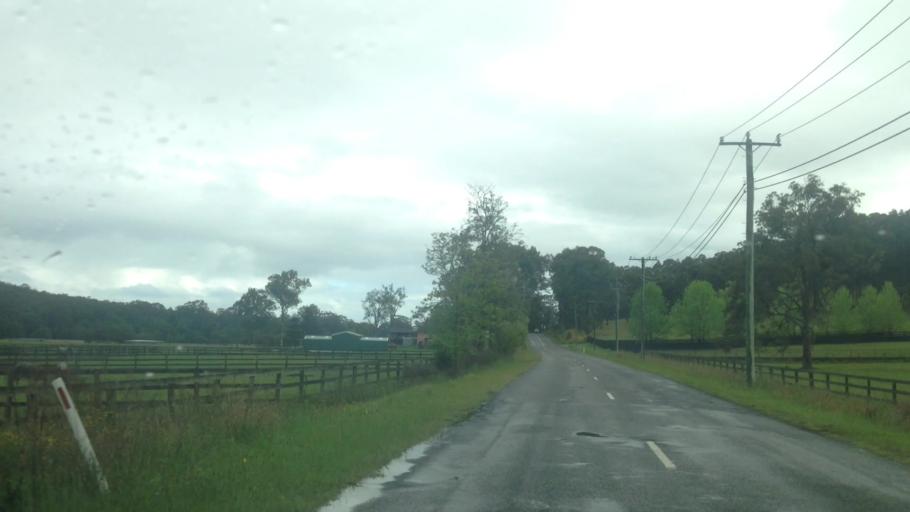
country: AU
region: New South Wales
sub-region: Wyong Shire
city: Little Jilliby
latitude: -33.2432
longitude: 151.3822
